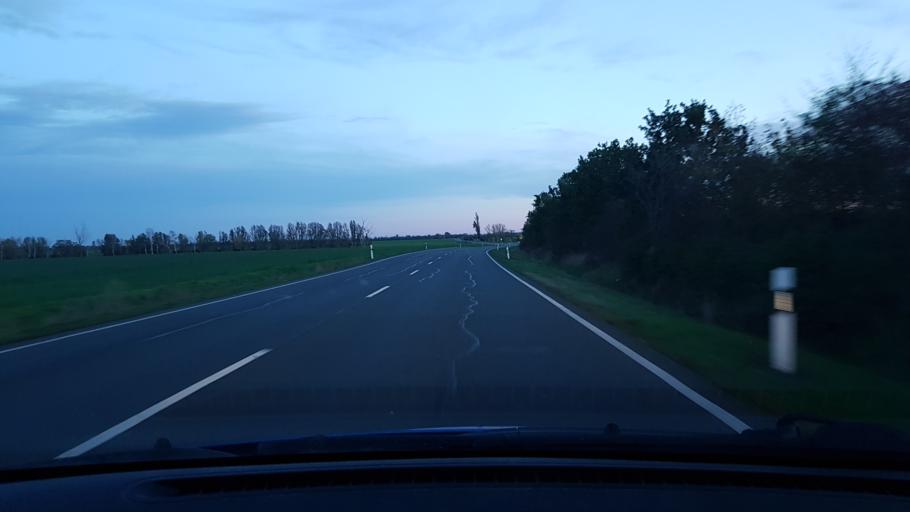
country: DE
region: Saxony-Anhalt
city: Zerbst
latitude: 52.0028
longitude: 12.0295
